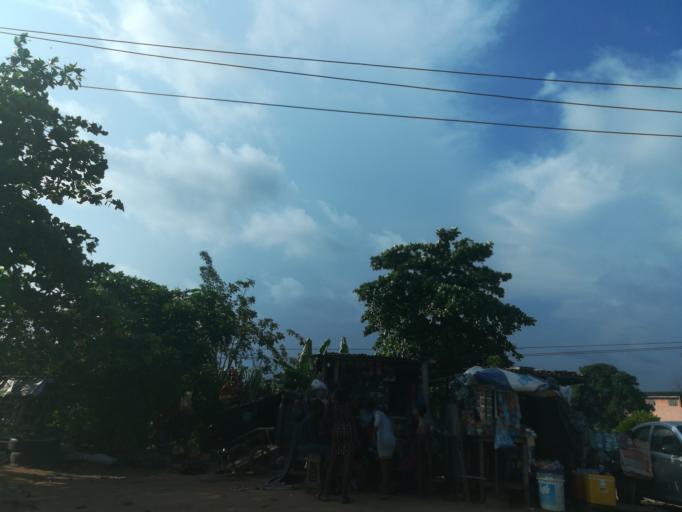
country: NG
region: Ogun
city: Ado Odo
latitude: 6.4953
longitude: 3.0844
